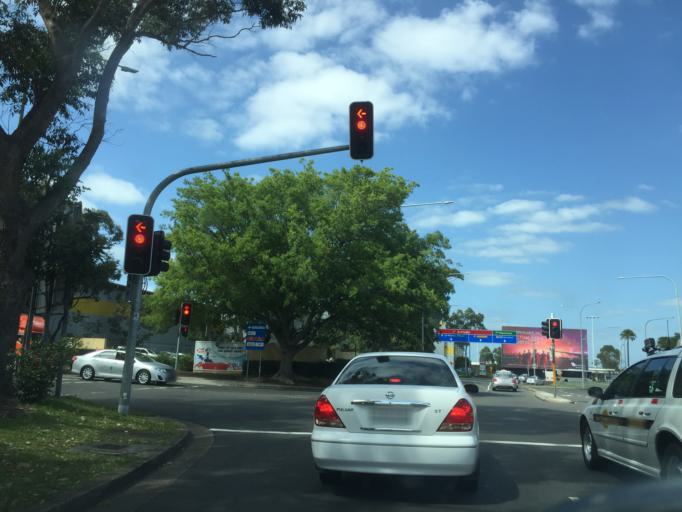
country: AU
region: New South Wales
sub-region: Botany Bay
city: Mascot
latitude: -33.9328
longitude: 151.1861
